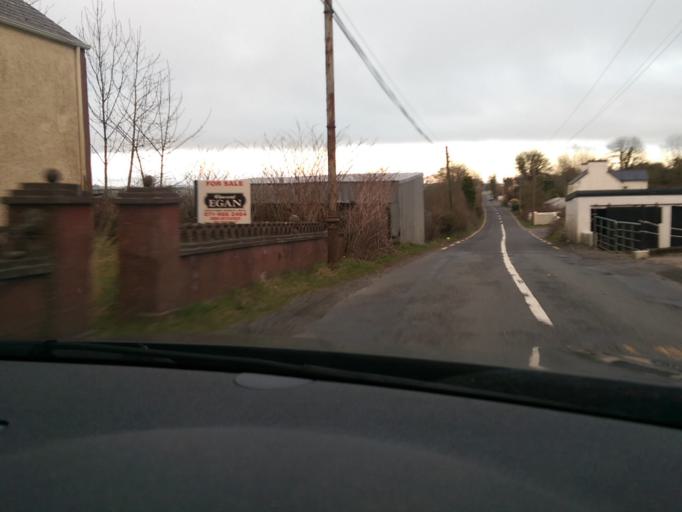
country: IE
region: Connaught
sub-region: Sligo
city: Ballymote
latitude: 53.9909
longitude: -8.5088
